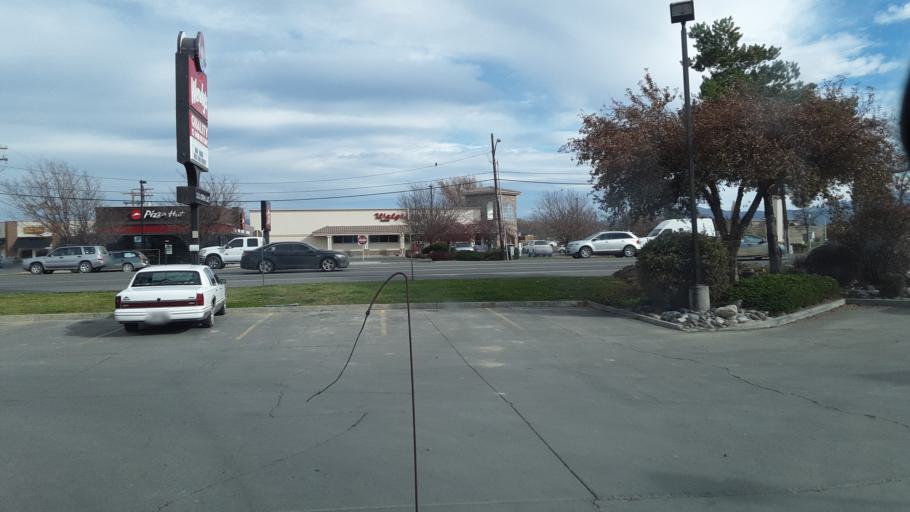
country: US
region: Colorado
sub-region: Montrose County
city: Montrose
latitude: 38.4605
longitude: -107.8667
